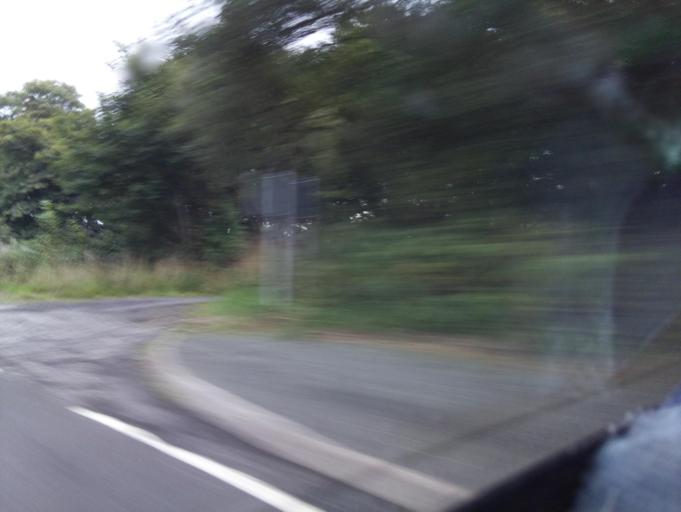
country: GB
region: Scotland
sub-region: Clackmannanshire
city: Dollar
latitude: 56.1841
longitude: -3.6231
